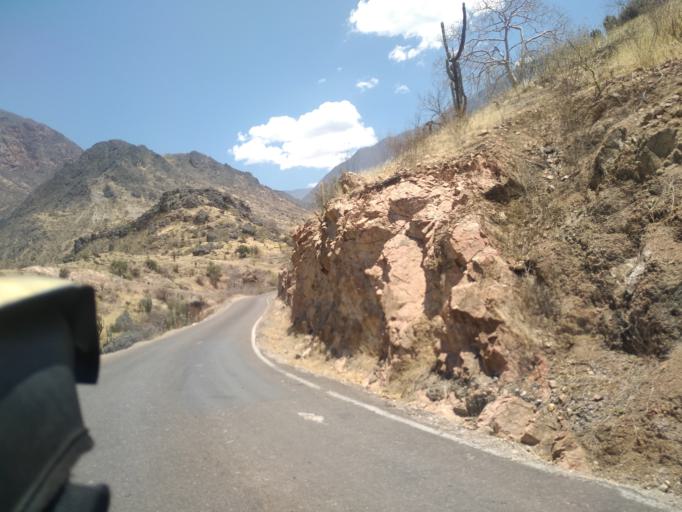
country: PE
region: Amazonas
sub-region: Provincia de Chachapoyas
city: Balsas
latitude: -6.8539
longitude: -78.0275
